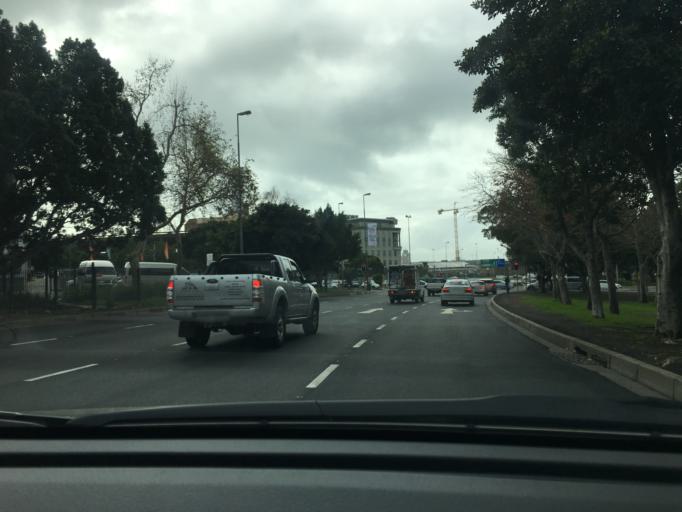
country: ZA
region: Western Cape
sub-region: City of Cape Town
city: Cape Town
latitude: -33.9164
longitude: 18.4214
